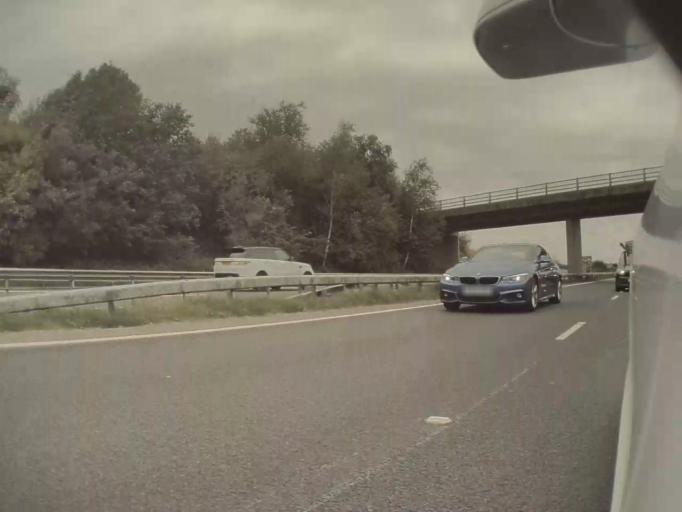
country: GB
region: Wales
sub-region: Anglesey
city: Llanfachraeth
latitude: 53.2570
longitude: -4.4411
